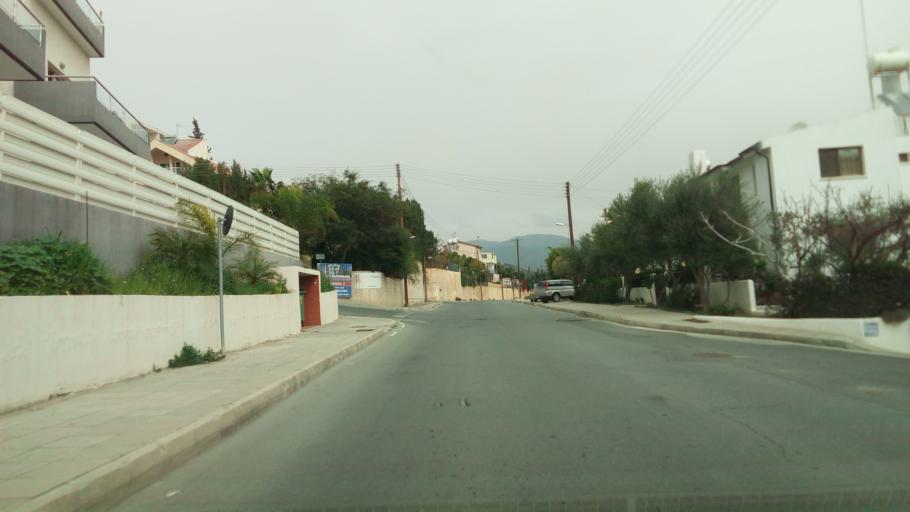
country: CY
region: Limassol
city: Mouttagiaka
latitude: 34.7279
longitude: 33.0840
